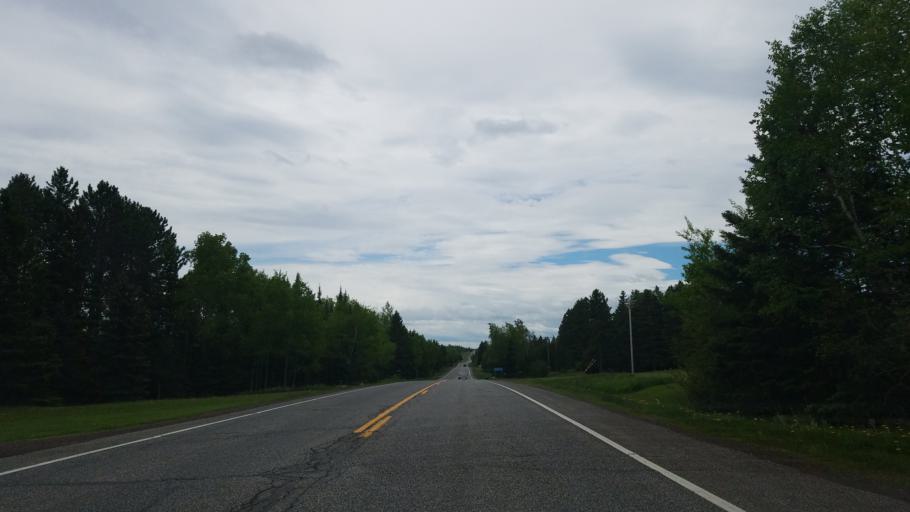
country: US
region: Minnesota
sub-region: Lake County
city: Two Harbors
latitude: 47.0443
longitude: -91.6358
